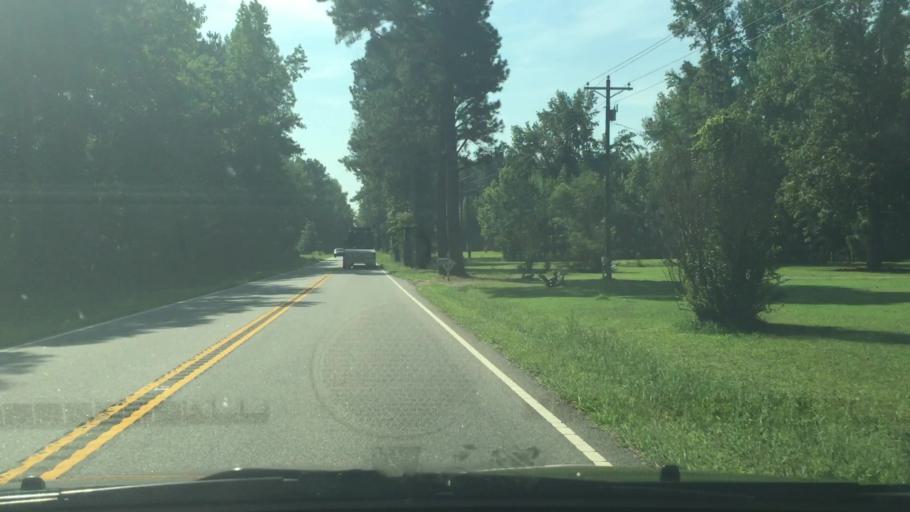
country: US
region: Virginia
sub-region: Sussex County
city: Sussex
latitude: 37.0233
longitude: -77.2893
